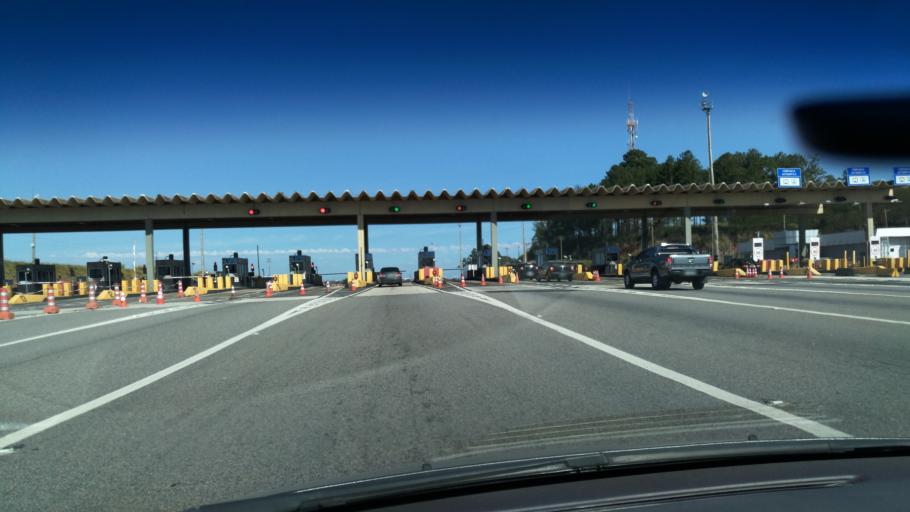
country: BR
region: Sao Paulo
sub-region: Jaguariuna
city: Jaguariuna
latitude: -22.7706
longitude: -47.0221
